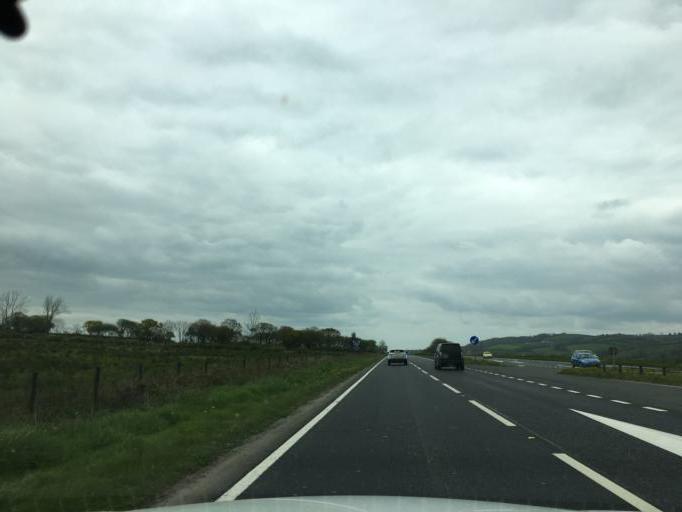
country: GB
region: Wales
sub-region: Carmarthenshire
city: Llangynog
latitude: 51.8283
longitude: -4.4490
